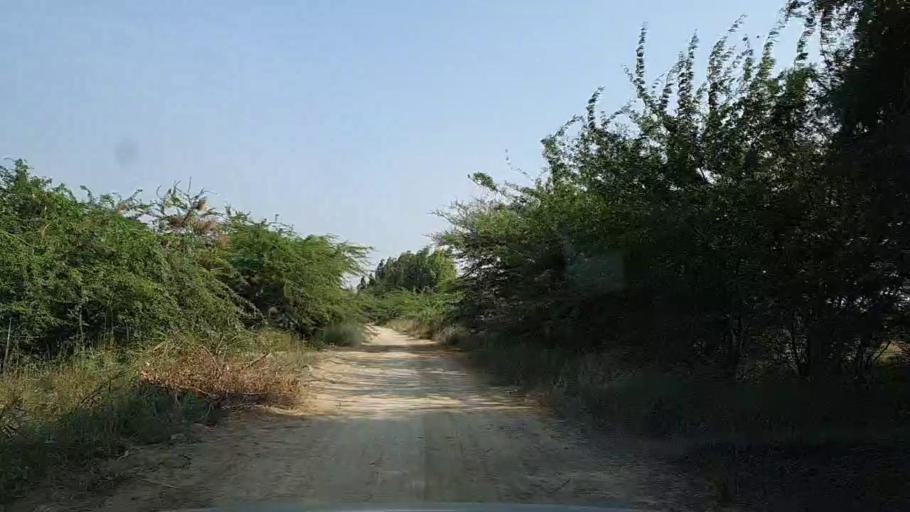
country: PK
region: Sindh
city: Mirpur Sakro
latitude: 24.5525
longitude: 67.5623
